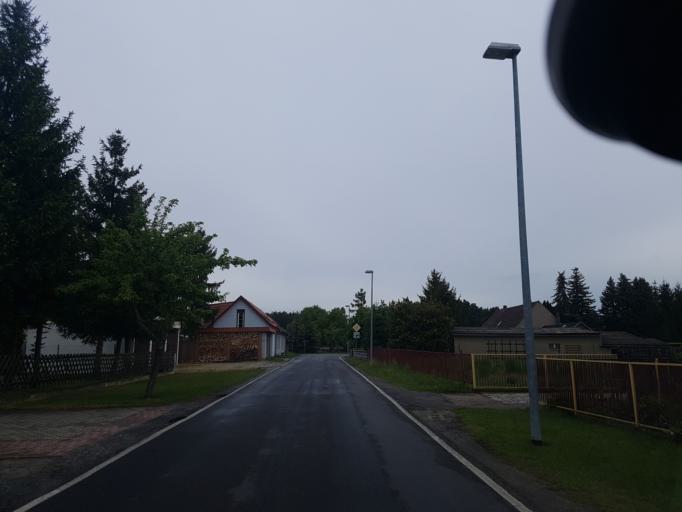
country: DE
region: Brandenburg
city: Spremberg
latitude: 51.6736
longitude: 14.4405
